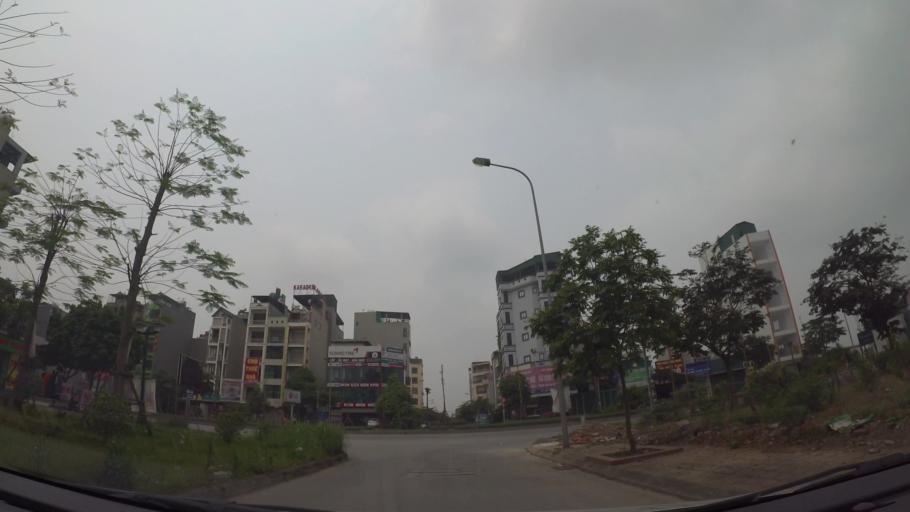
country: VN
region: Ha Noi
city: Ha Dong
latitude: 20.9727
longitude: 105.7484
